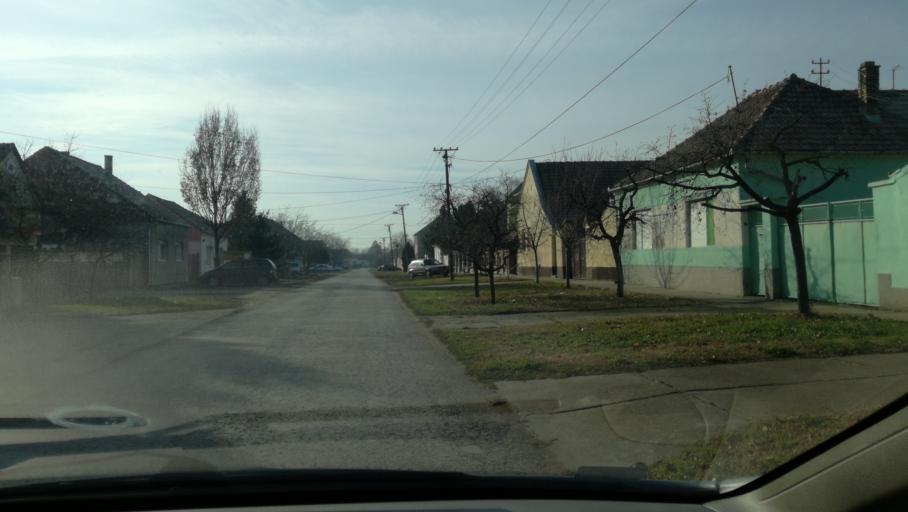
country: RS
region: Autonomna Pokrajina Vojvodina
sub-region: Severnobanatski Okrug
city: Kikinda
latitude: 45.8397
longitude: 20.4723
